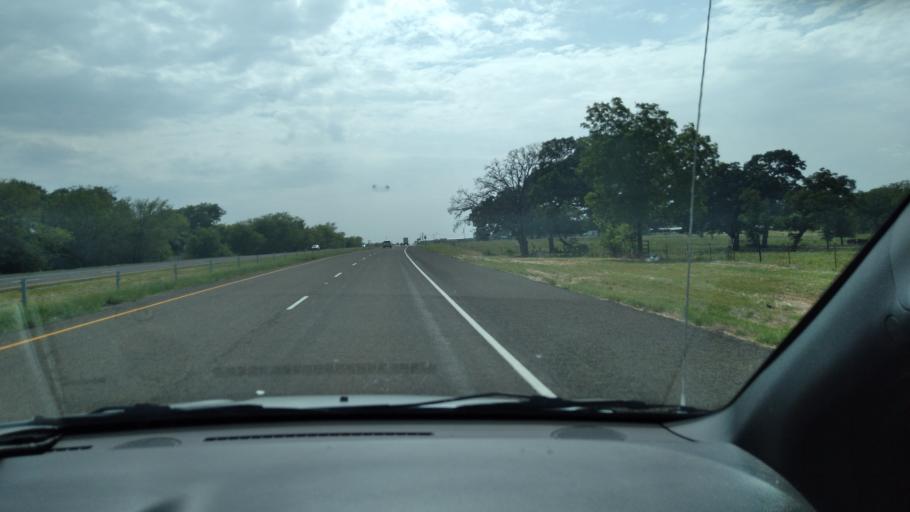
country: US
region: Texas
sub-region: Navarro County
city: Kerens
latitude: 32.1234
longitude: -96.2884
